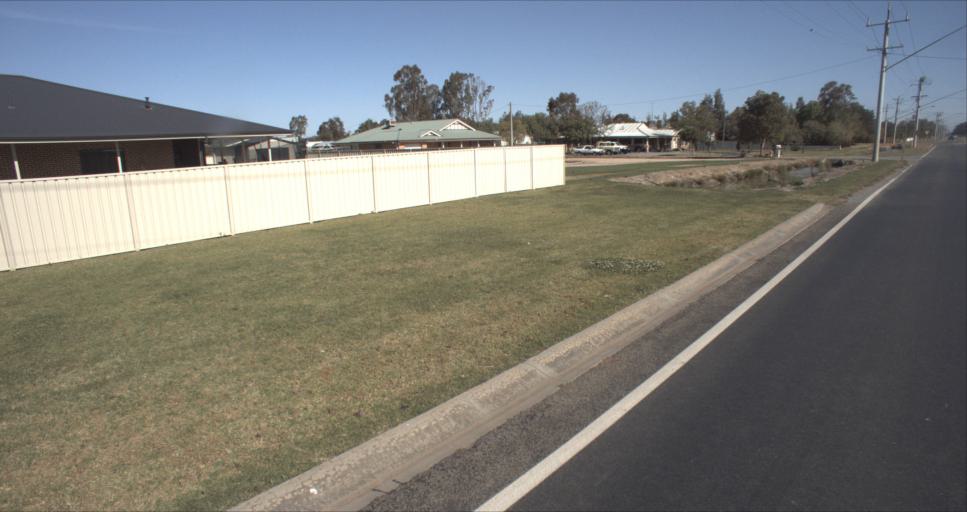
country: AU
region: New South Wales
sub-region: Leeton
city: Leeton
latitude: -34.5553
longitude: 146.4164
